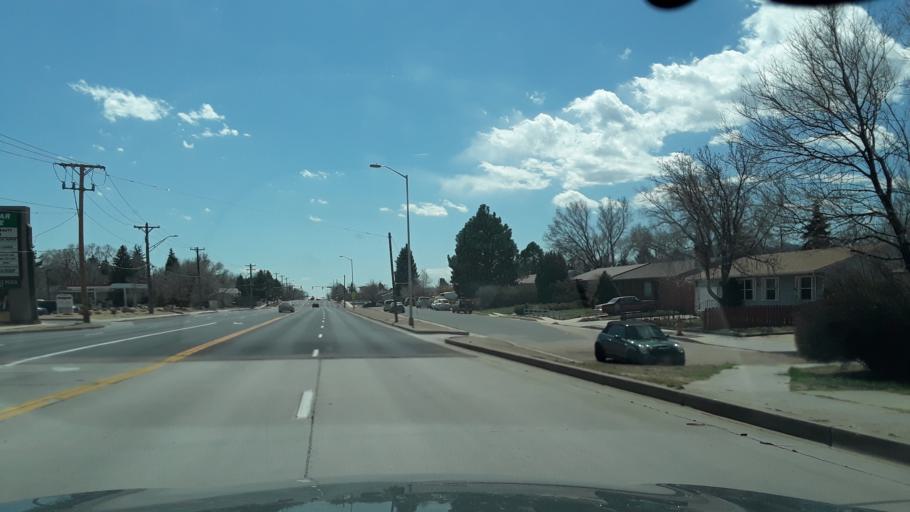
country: US
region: Colorado
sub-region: El Paso County
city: Colorado Springs
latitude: 38.8590
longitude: -104.7758
